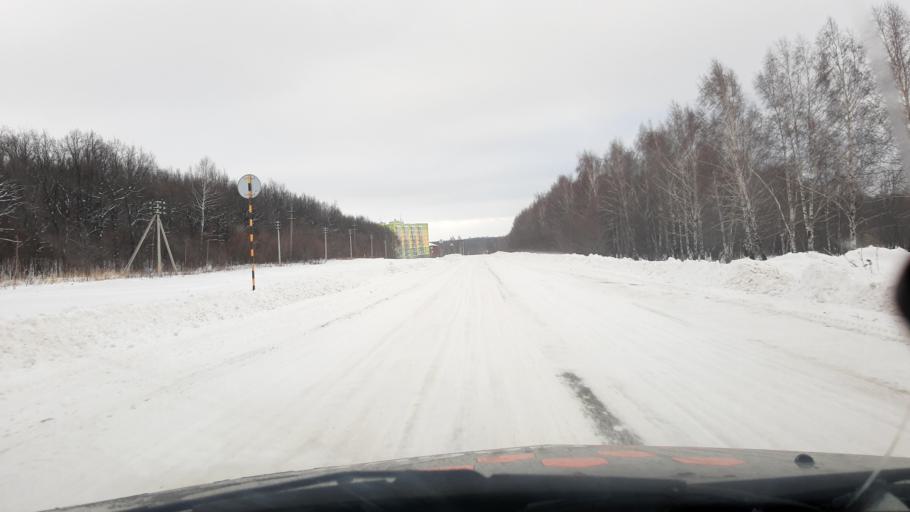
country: RU
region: Bashkortostan
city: Avdon
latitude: 54.6749
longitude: 55.7048
